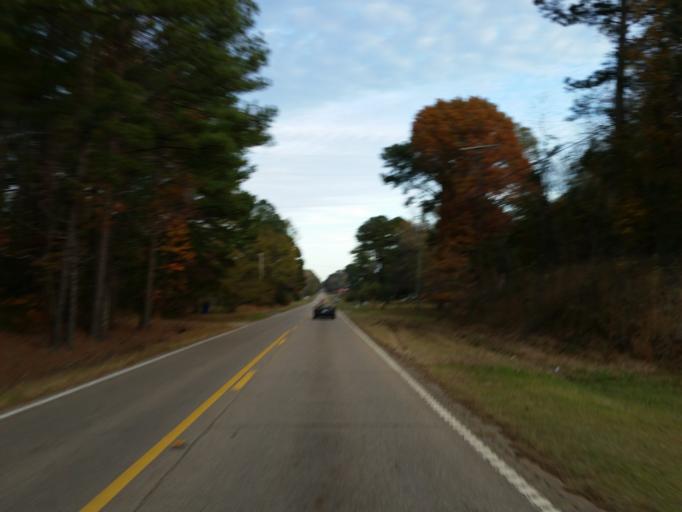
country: US
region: Mississippi
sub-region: Lauderdale County
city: Marion
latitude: 32.4197
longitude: -88.5310
